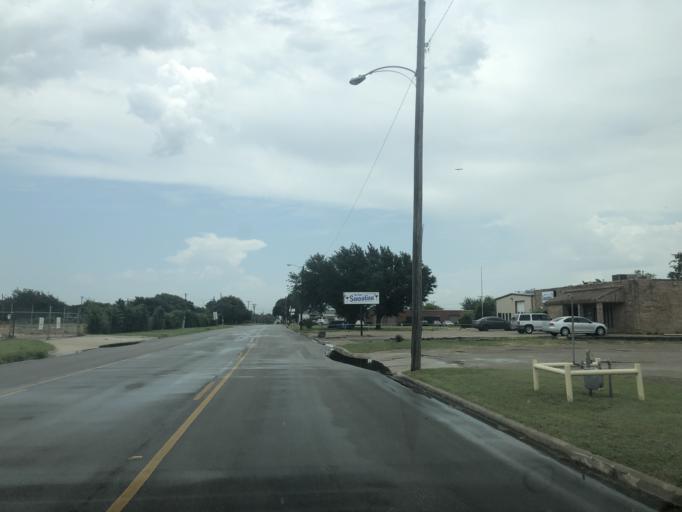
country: US
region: Texas
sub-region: Dallas County
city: Grand Prairie
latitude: 32.7446
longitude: -97.0423
